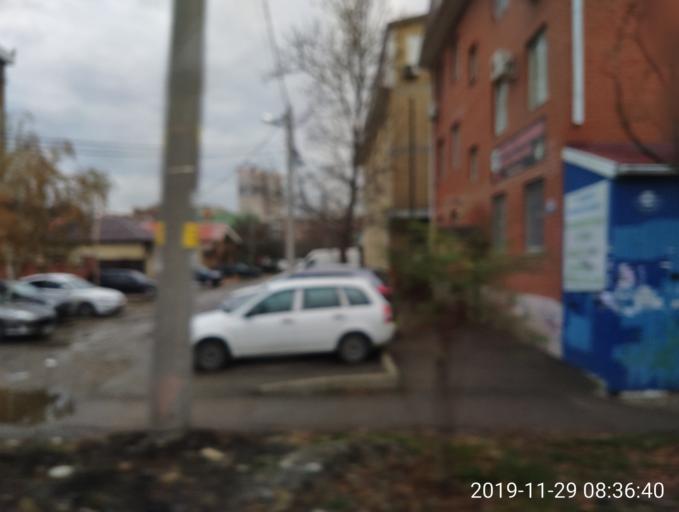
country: RU
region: Krasnodarskiy
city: Krasnodar
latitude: 45.0540
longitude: 39.0027
